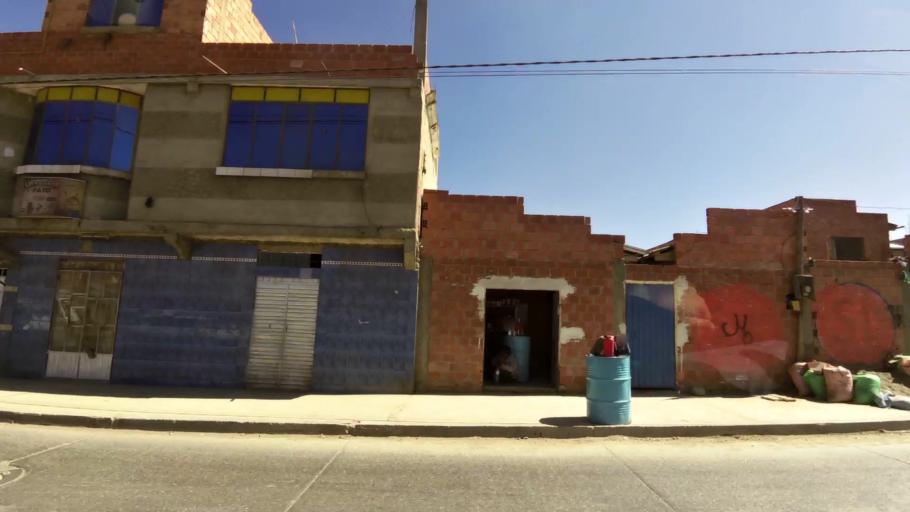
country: BO
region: La Paz
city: La Paz
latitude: -16.4943
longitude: -68.2048
